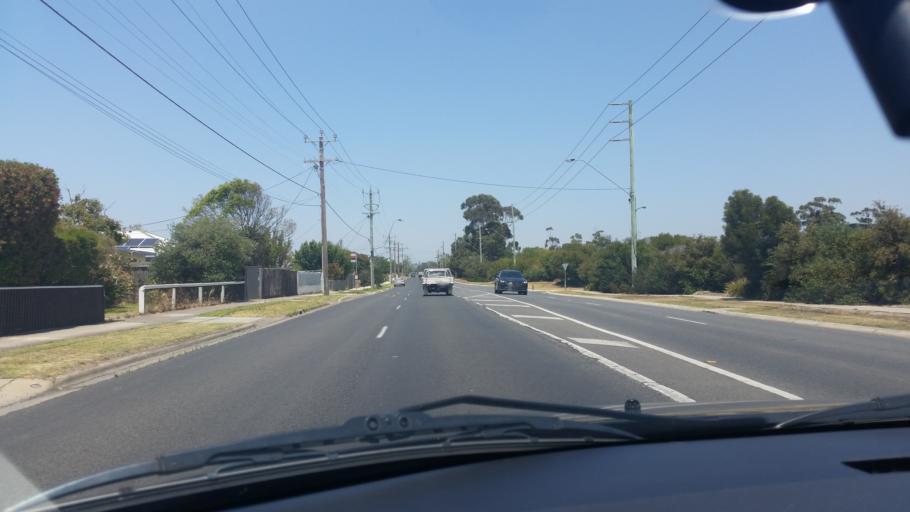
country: AU
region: Victoria
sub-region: Greater Geelong
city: Bell Park
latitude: -38.1176
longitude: 144.3421
